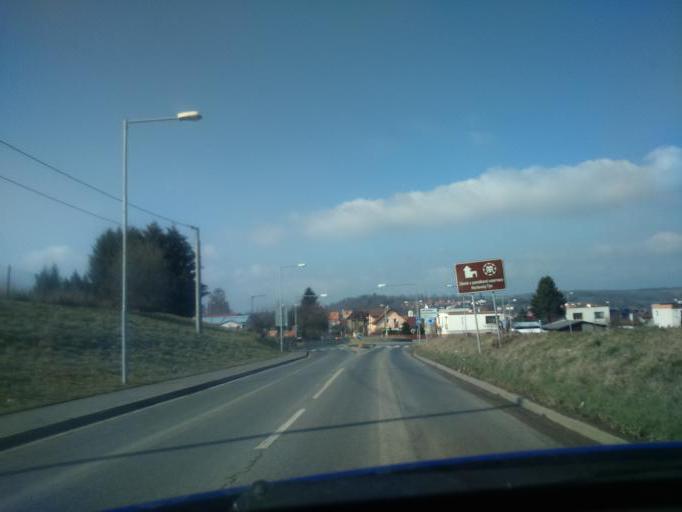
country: CZ
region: Plzensky
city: Horsovsky Tyn
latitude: 49.5214
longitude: 12.9474
